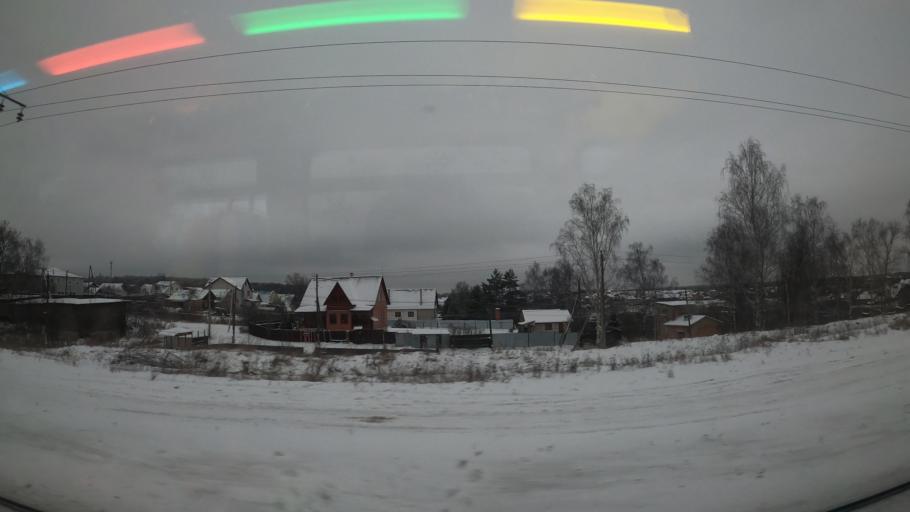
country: RU
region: Vladimir
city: Aleksandrov
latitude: 56.4063
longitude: 38.7324
